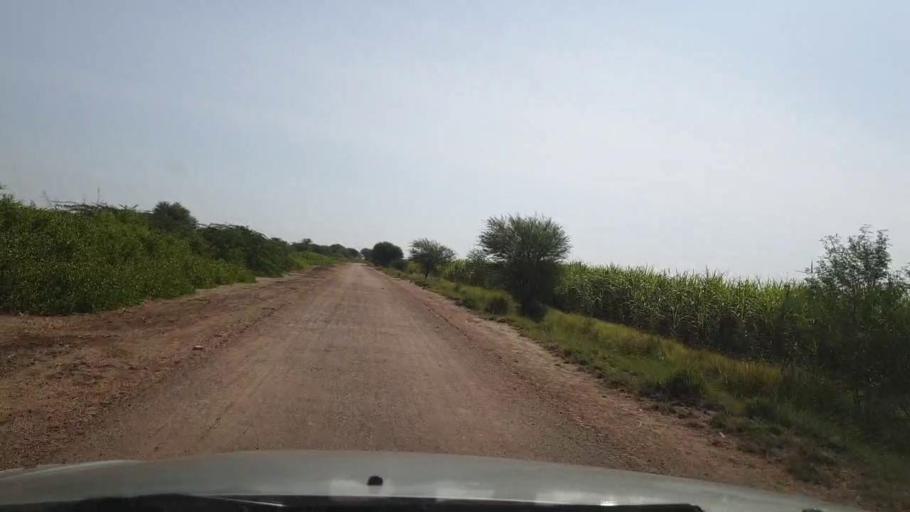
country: PK
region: Sindh
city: Bulri
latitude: 25.0144
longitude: 68.3197
